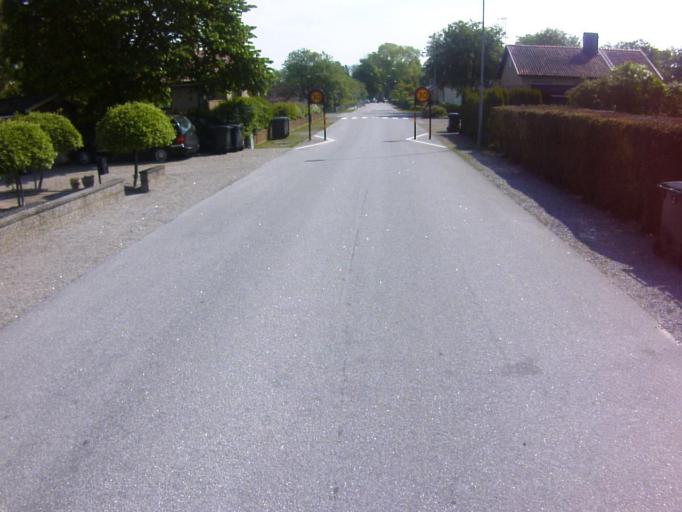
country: SE
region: Blekinge
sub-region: Solvesborgs Kommun
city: Soelvesborg
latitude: 56.0477
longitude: 14.6744
